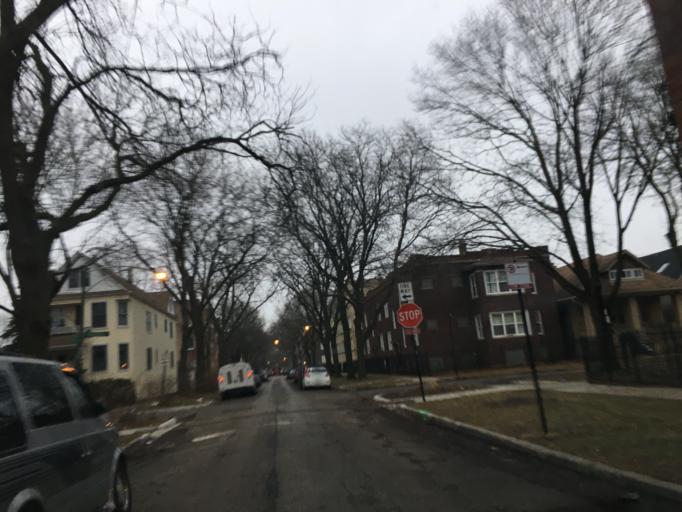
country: US
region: Illinois
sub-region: Cook County
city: Lincolnwood
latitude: 41.9630
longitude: -87.7148
